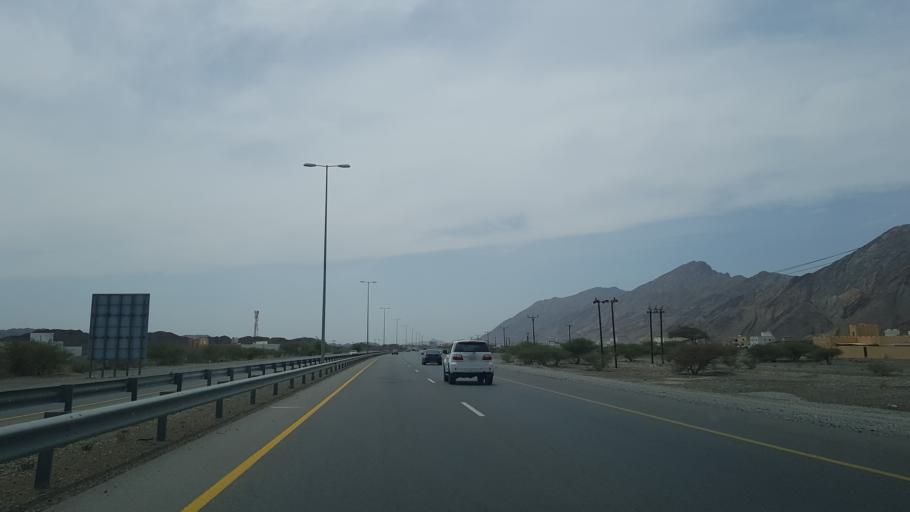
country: OM
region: Muhafazat ad Dakhiliyah
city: Izki
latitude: 23.0344
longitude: 57.7996
